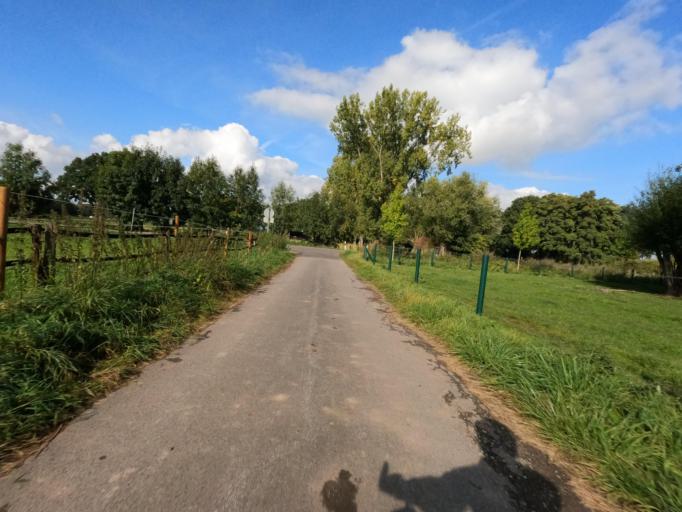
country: DE
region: North Rhine-Westphalia
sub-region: Regierungsbezirk Koln
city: Linnich
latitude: 51.0005
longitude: 6.2552
